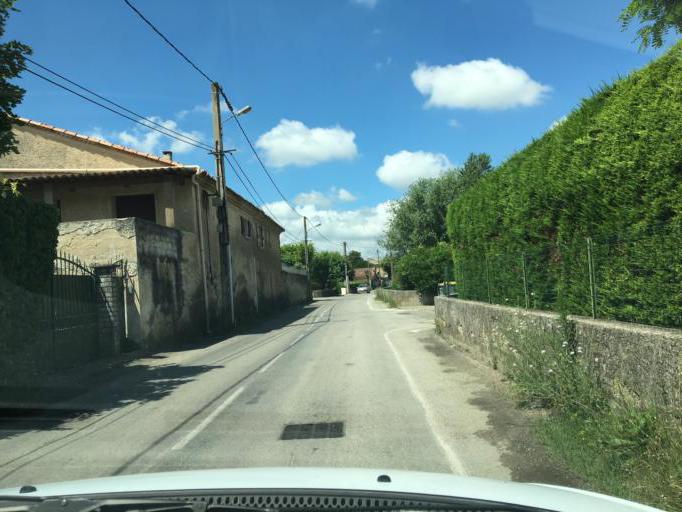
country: FR
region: Provence-Alpes-Cote d'Azur
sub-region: Departement du Vaucluse
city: Carpentras
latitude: 44.0510
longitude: 5.0588
